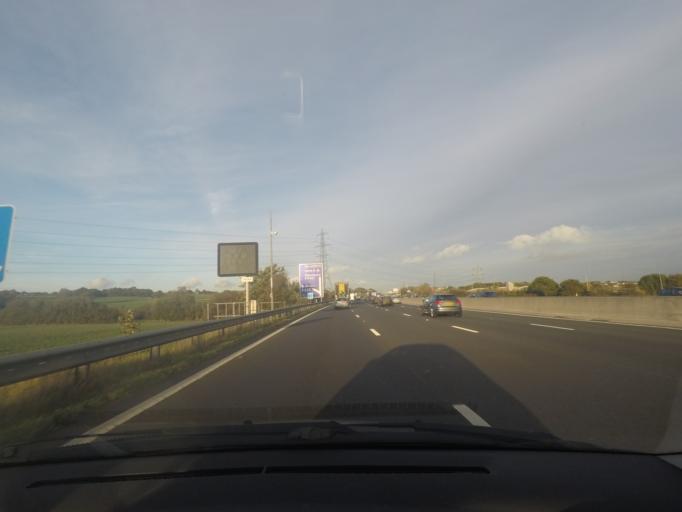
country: GB
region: England
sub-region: City and Borough of Wakefield
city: Ossett
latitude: 53.7118
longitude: -1.5451
